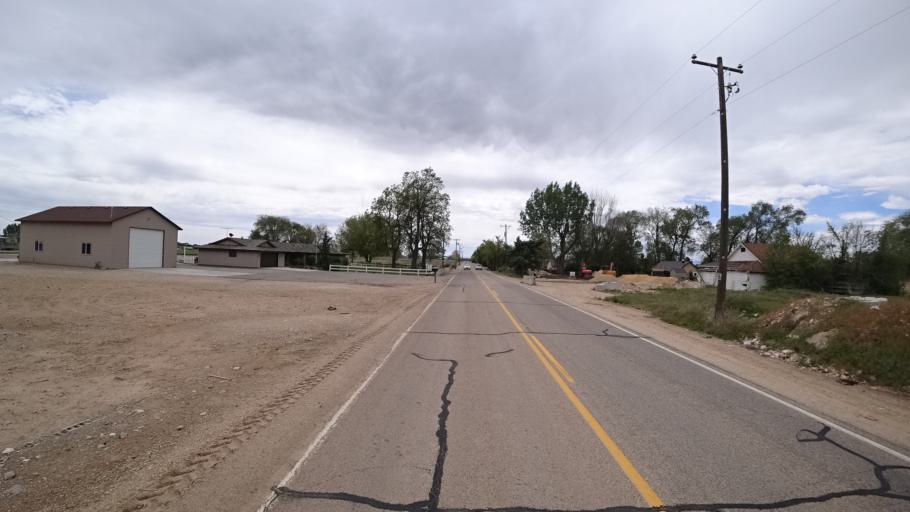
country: US
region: Idaho
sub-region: Ada County
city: Meridian
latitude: 43.5547
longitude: -116.4138
